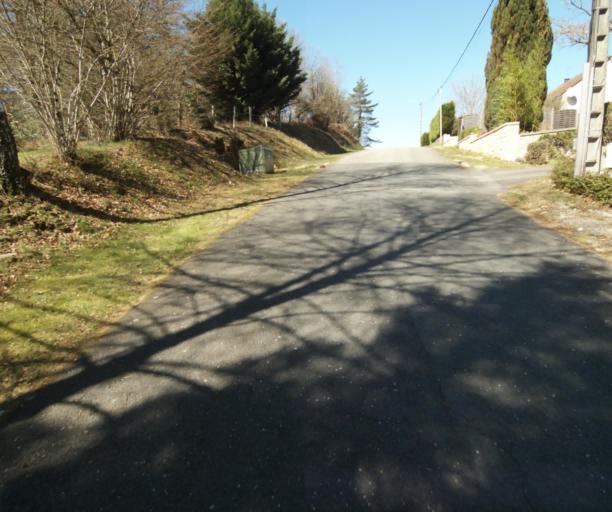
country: FR
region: Limousin
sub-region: Departement de la Correze
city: Seilhac
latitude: 45.3717
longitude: 1.6902
